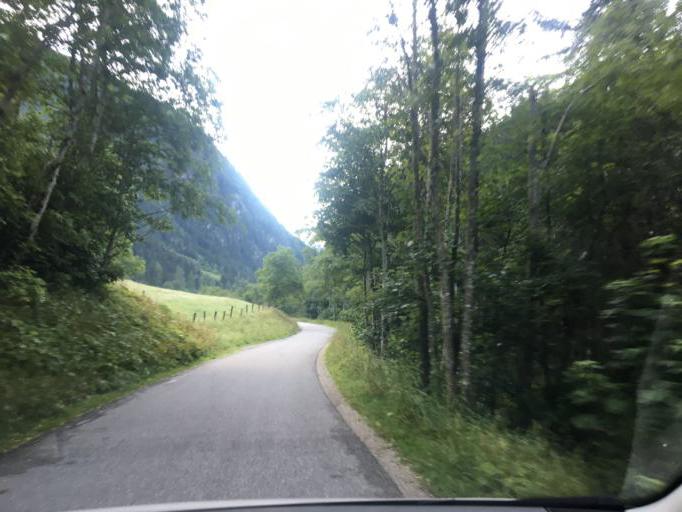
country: AT
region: Styria
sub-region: Politischer Bezirk Liezen
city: Schladming
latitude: 47.3363
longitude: 13.6801
